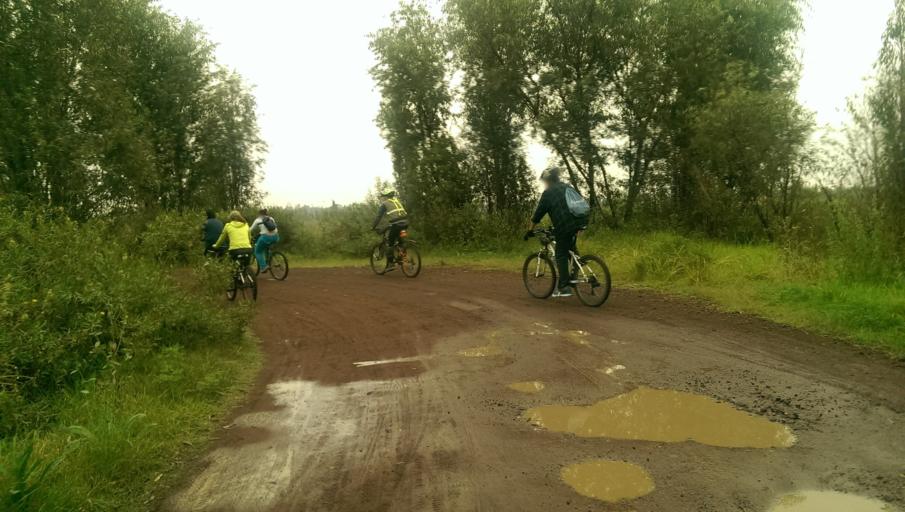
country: MX
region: Mexico City
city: Xochimilco
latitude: 19.2748
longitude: -99.0757
